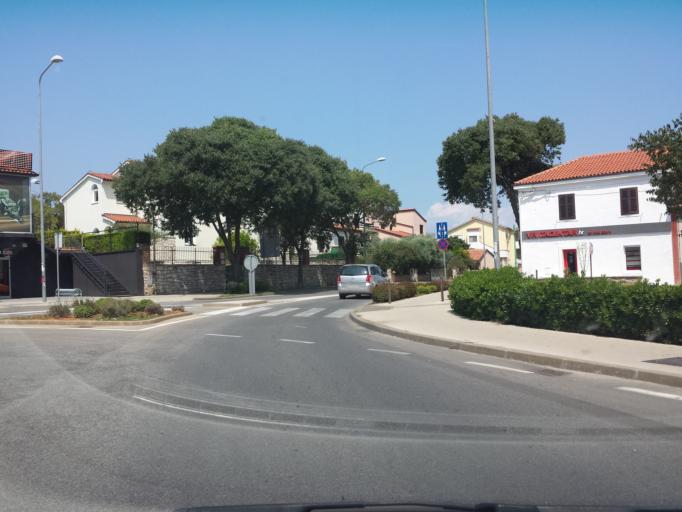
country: HR
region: Istarska
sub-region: Grad Pula
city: Pula
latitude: 44.8784
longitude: 13.8615
